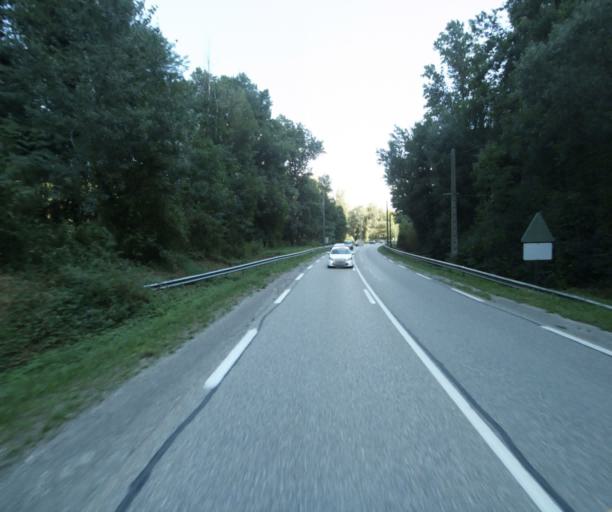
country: FR
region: Rhone-Alpes
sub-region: Departement de l'Isere
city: Voreppe
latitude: 45.2956
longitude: 5.6130
